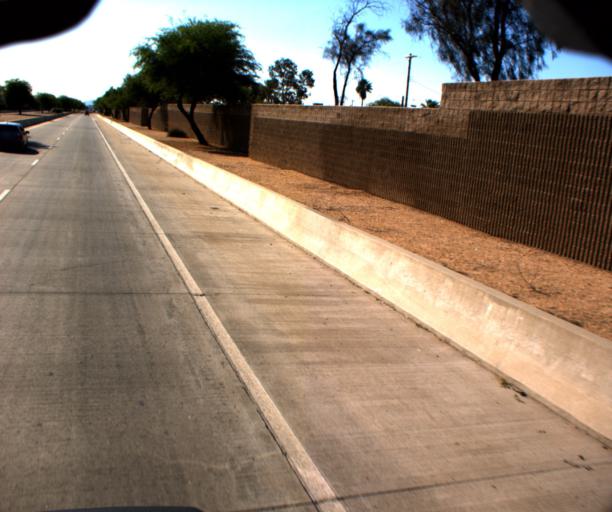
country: US
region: Arizona
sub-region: Pima County
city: Tucson
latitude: 32.1951
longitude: -110.9224
